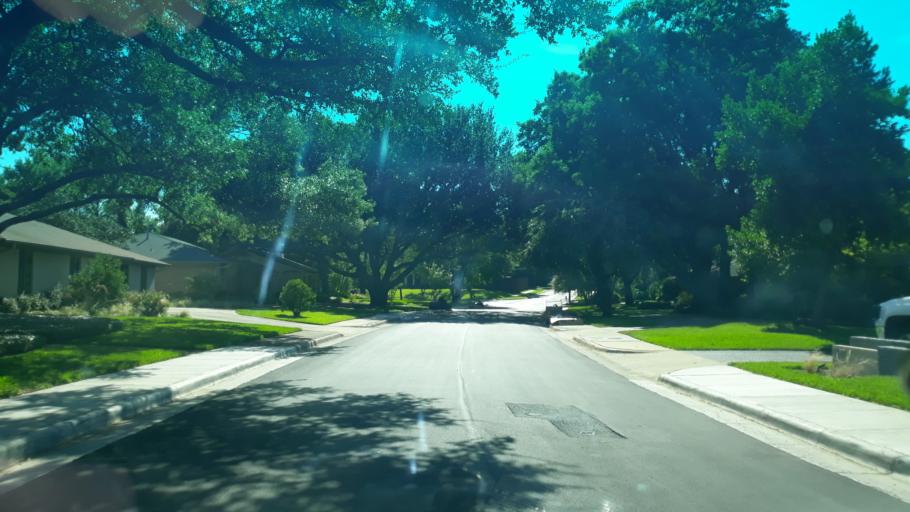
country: US
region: Texas
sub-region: Dallas County
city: Highland Park
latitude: 32.8211
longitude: -96.7474
